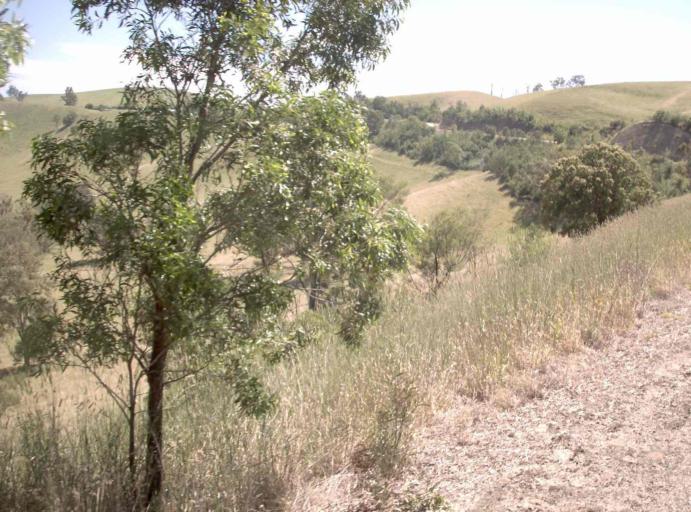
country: AU
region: Victoria
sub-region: East Gippsland
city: Lakes Entrance
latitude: -37.4923
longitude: 148.1837
